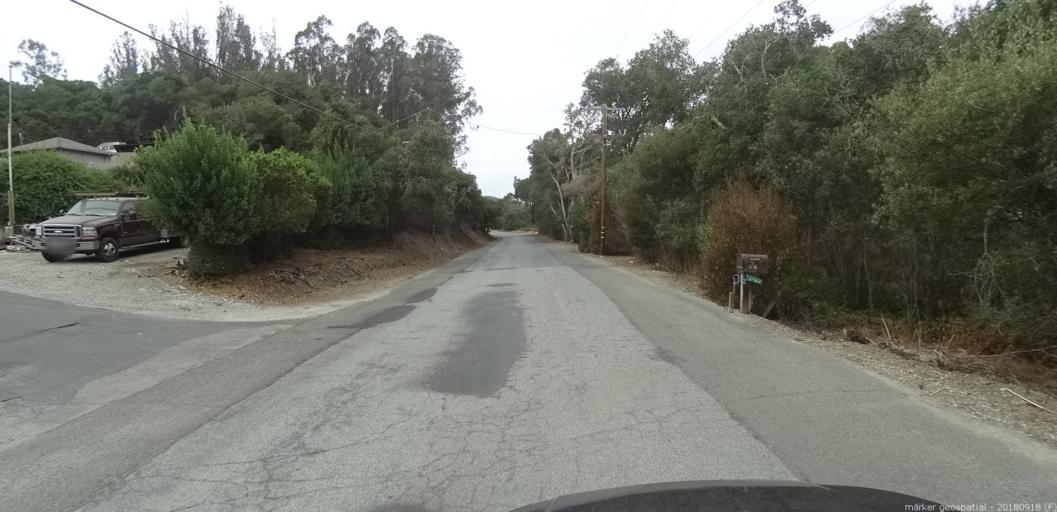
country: US
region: California
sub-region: Monterey County
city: Prunedale
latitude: 36.7822
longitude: -121.6357
